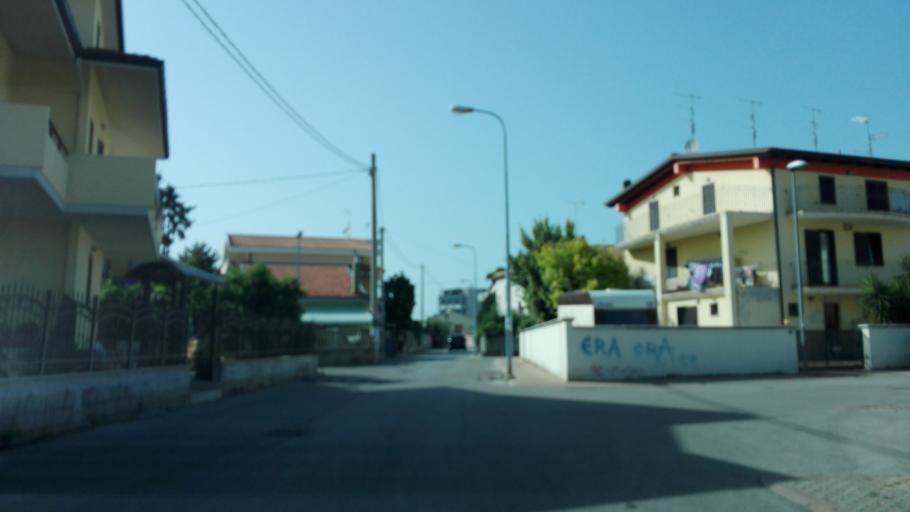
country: IT
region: Abruzzo
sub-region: Provincia di Pescara
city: Montesilvano Marina
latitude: 42.5086
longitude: 14.1397
